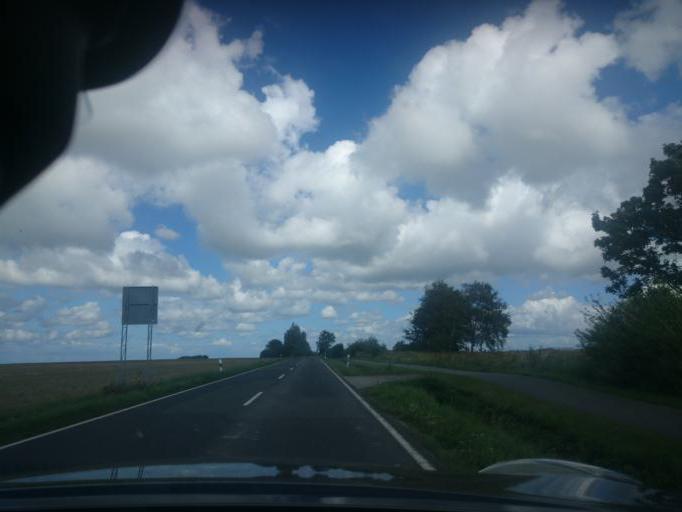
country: DE
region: Mecklenburg-Vorpommern
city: Saal
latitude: 54.3150
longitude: 12.4980
